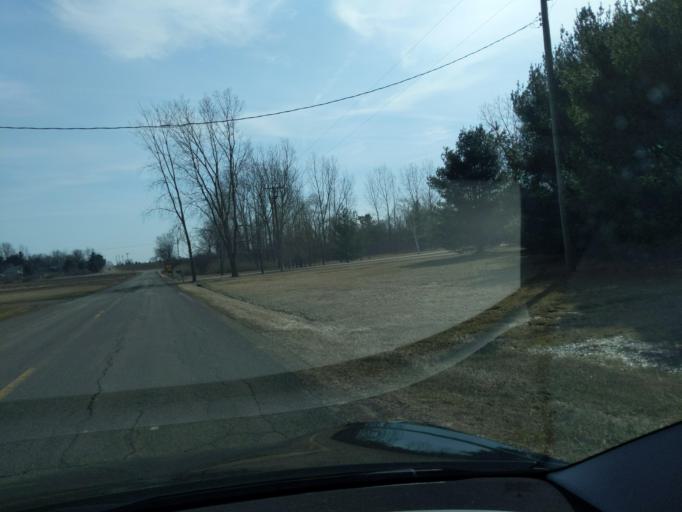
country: US
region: Michigan
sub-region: Ingham County
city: Williamston
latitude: 42.6587
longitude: -84.2659
